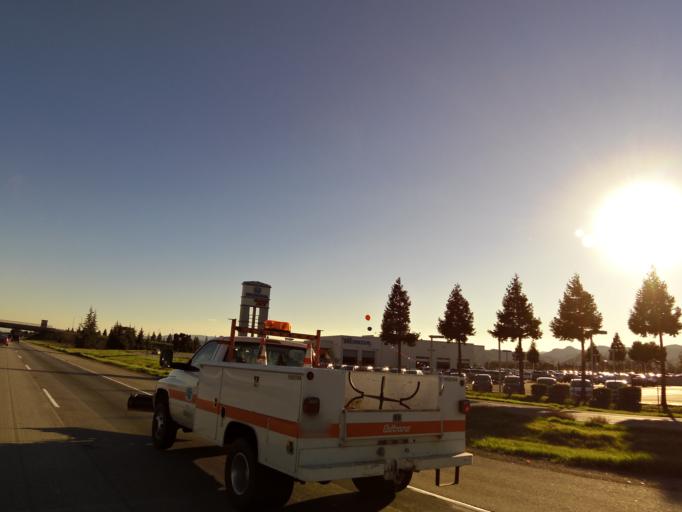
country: US
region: California
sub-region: Santa Clara County
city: Morgan Hill
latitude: 37.1344
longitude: -121.6354
